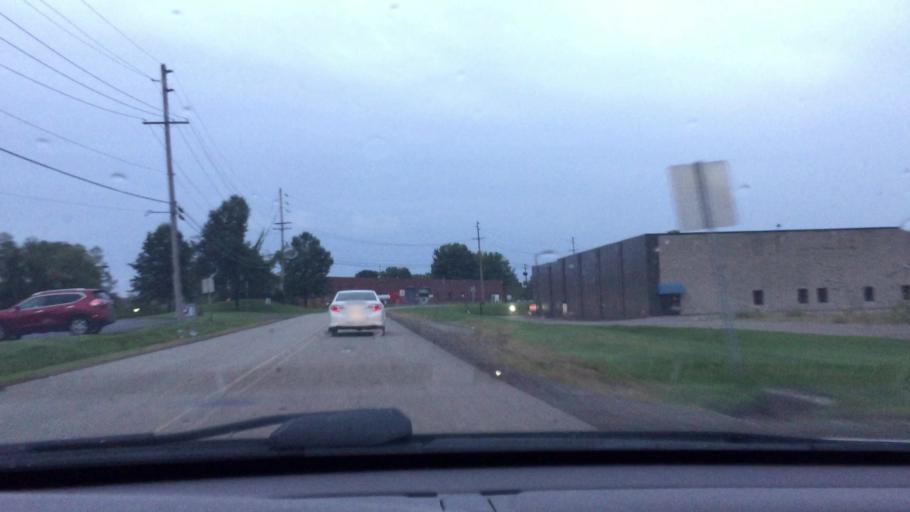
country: US
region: Pennsylvania
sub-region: Allegheny County
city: Cheswick
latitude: 40.5587
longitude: -79.8246
